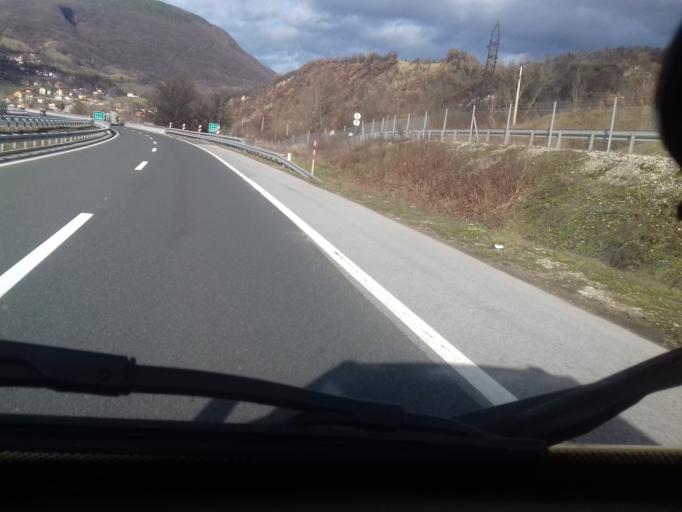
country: BA
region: Federation of Bosnia and Herzegovina
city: Kakanj
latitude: 44.1329
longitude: 18.0846
